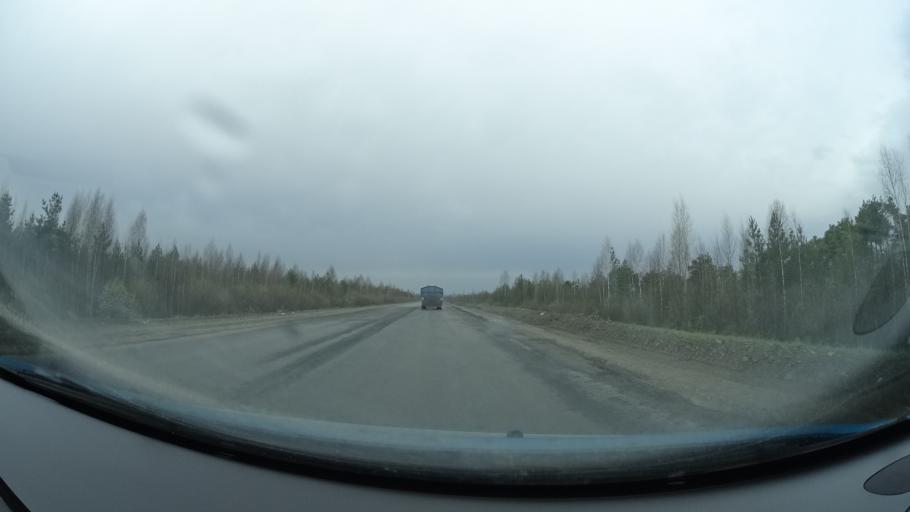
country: RU
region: Perm
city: Krasnokamsk
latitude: 58.0875
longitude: 55.7002
